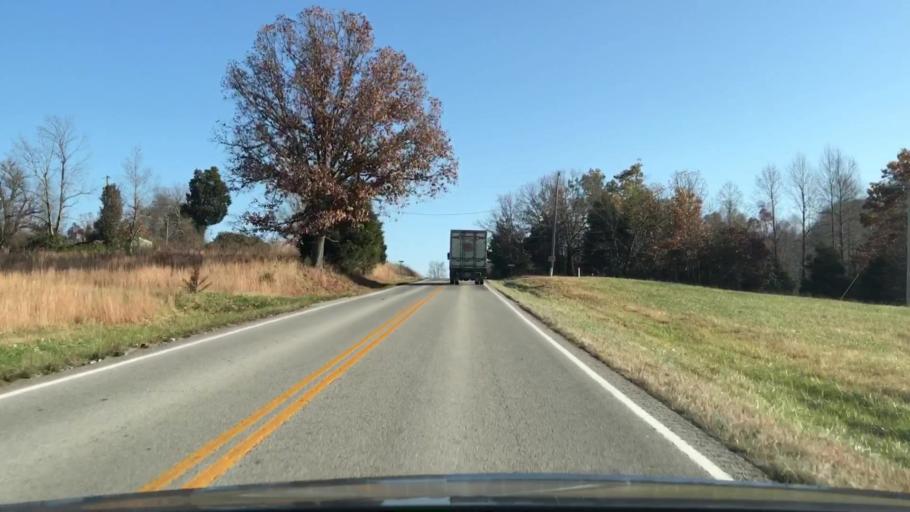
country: US
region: Kentucky
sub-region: Grayson County
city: Leitchfield
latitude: 37.3870
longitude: -86.2494
